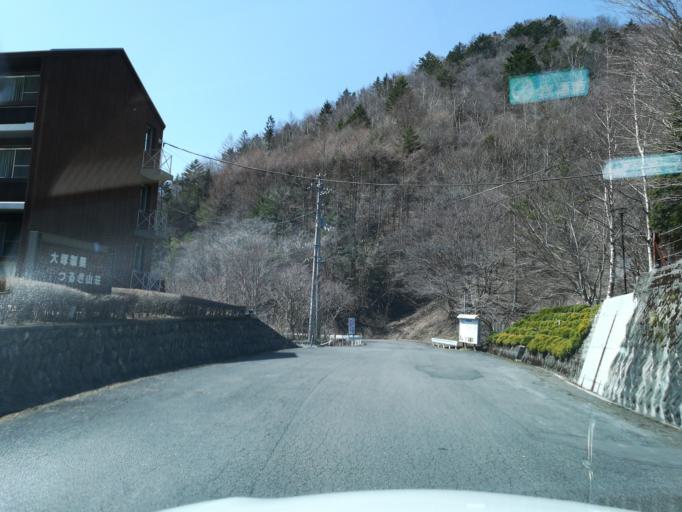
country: JP
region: Tokushima
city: Wakimachi
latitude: 33.8672
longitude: 134.0848
